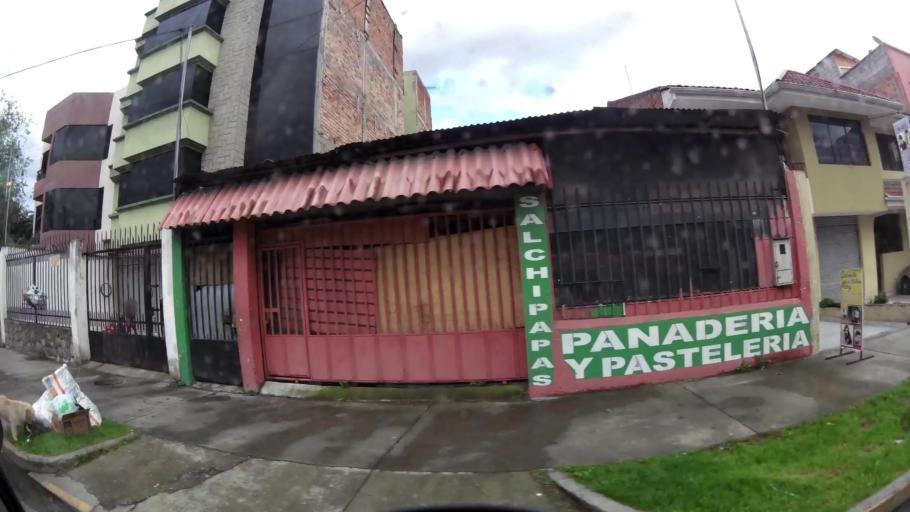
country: EC
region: Azuay
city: Cuenca
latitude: -2.8997
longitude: -79.0259
